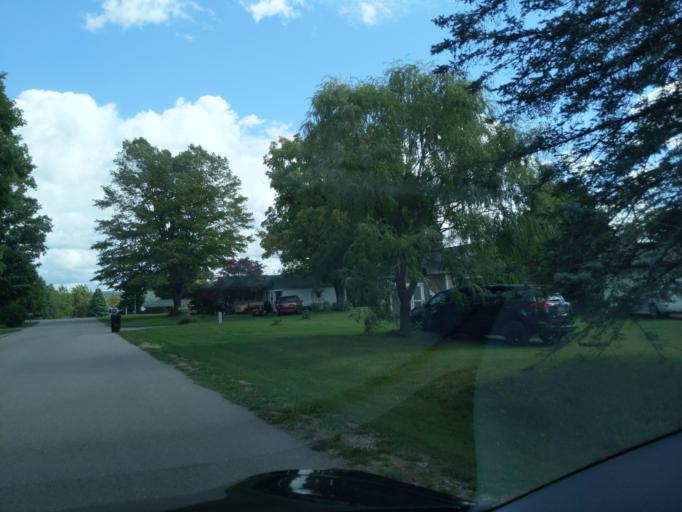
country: US
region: Michigan
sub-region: Antrim County
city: Bellaire
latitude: 45.0761
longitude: -85.3573
